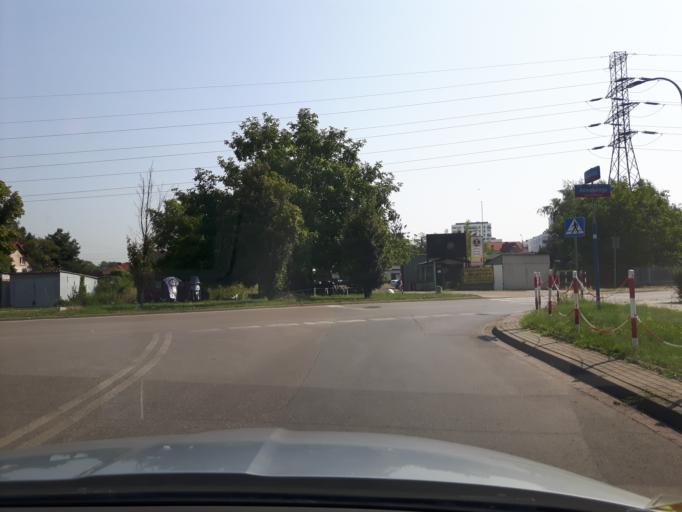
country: PL
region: Masovian Voivodeship
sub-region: Warszawa
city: Targowek
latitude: 52.2994
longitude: 21.0491
